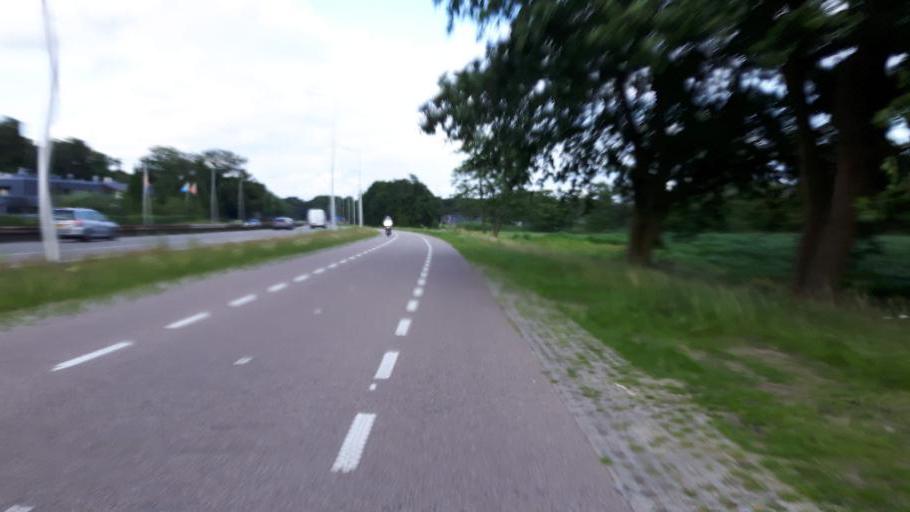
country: NL
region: Utrecht
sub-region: Gemeente De Bilt
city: De Bilt
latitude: 52.1019
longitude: 5.1904
